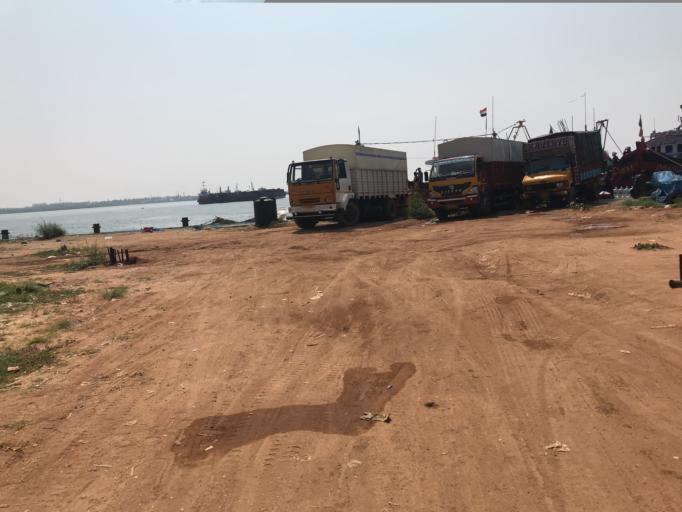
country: IN
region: Karnataka
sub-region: Dakshina Kannada
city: Ullal
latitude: 12.8499
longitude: 74.8327
